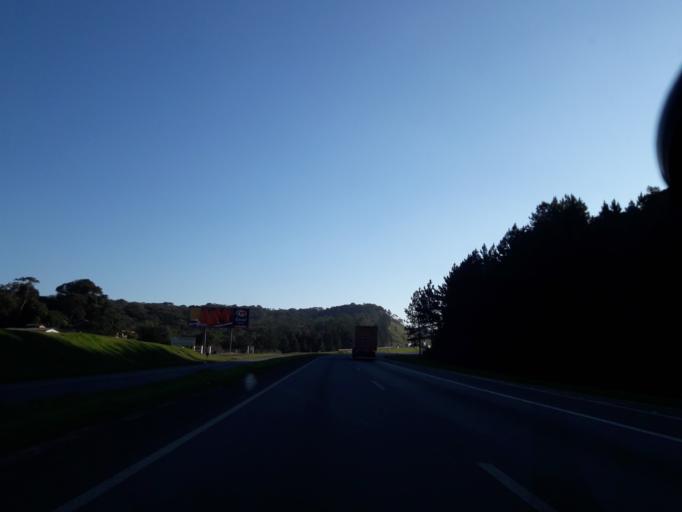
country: BR
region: Sao Paulo
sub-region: Juquitiba
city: Juquitiba
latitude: -23.9535
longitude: -47.1059
